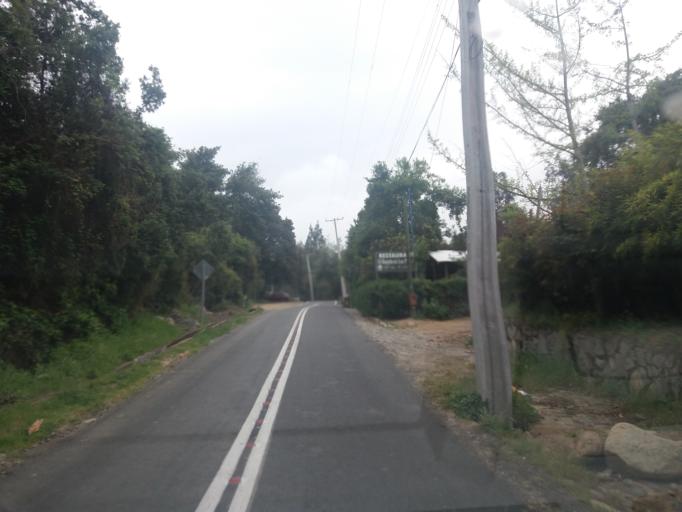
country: CL
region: Valparaiso
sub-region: Provincia de Marga Marga
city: Limache
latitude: -33.0221
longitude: -71.0718
